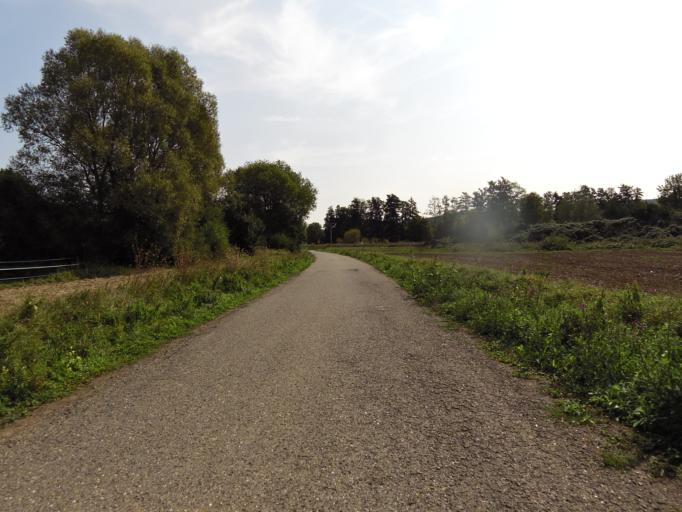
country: DE
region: Baden-Wuerttemberg
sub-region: Karlsruhe Region
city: Eschelbronn
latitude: 49.3252
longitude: 8.8576
